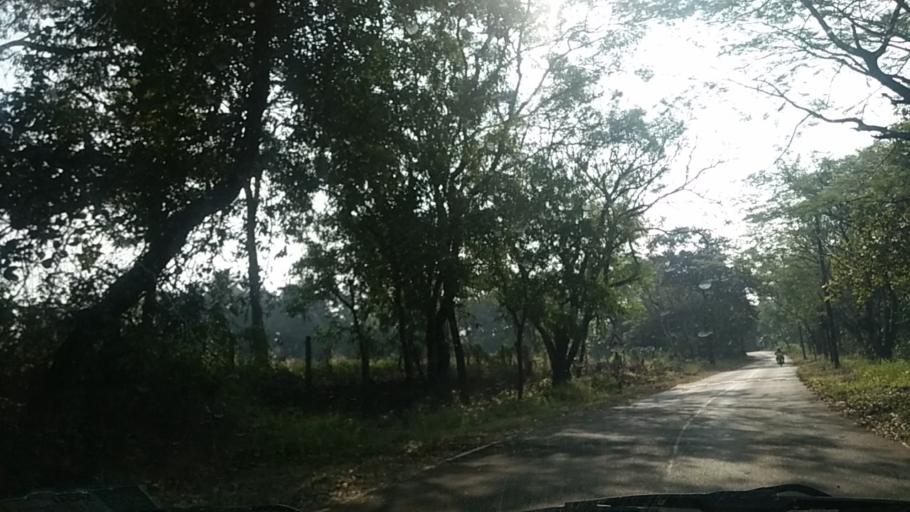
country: IN
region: Goa
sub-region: South Goa
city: Sanguem
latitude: 15.2113
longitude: 74.2157
